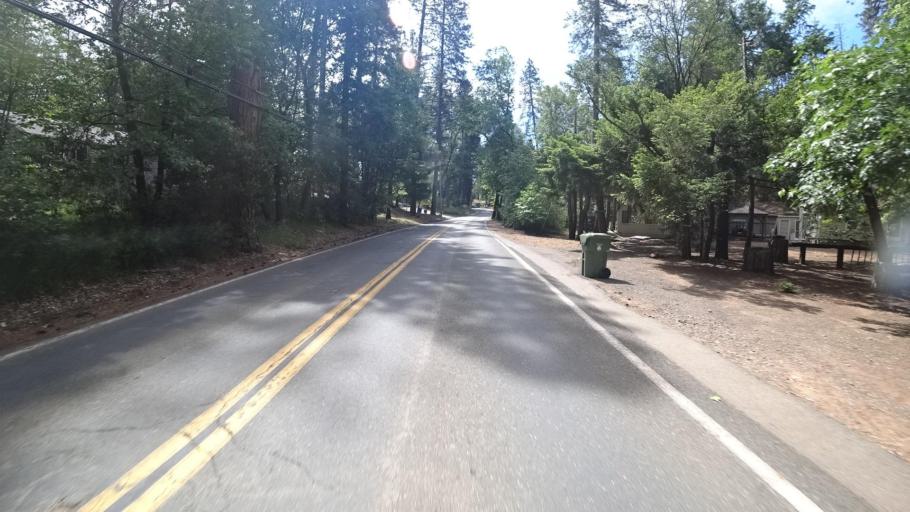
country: US
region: California
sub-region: Lake County
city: Cobb
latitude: 38.8619
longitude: -122.7149
